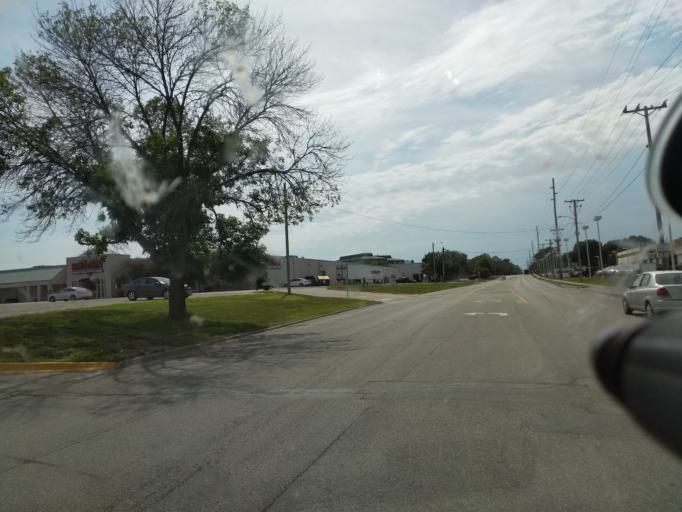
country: US
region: Iowa
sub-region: Polk County
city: Urbandale
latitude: 41.6367
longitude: -93.6988
